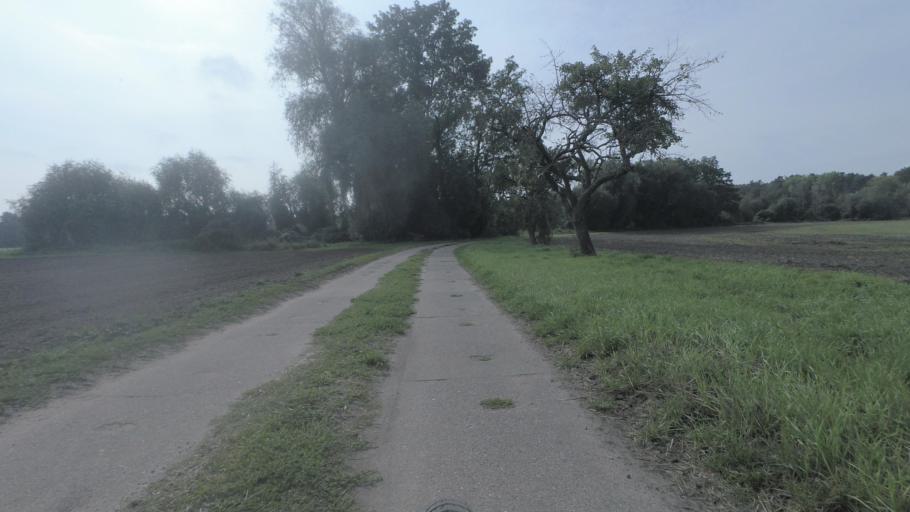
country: DE
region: Brandenburg
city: Rangsdorf
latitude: 52.2715
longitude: 13.3903
